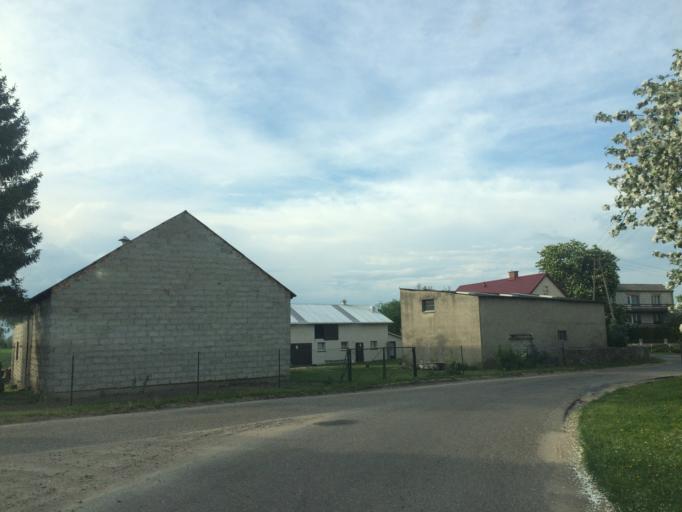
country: PL
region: Kujawsko-Pomorskie
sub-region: Powiat brodnicki
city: Brzozie
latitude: 53.3541
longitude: 19.6017
